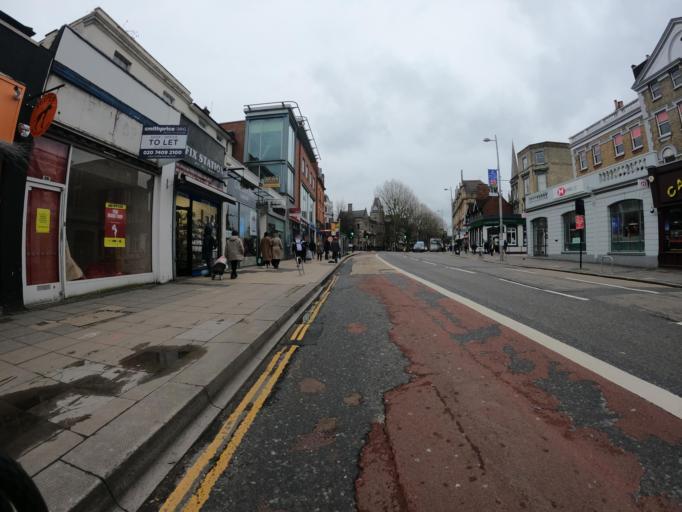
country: GB
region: England
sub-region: Greater London
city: Ealing
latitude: 51.5138
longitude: -0.3026
